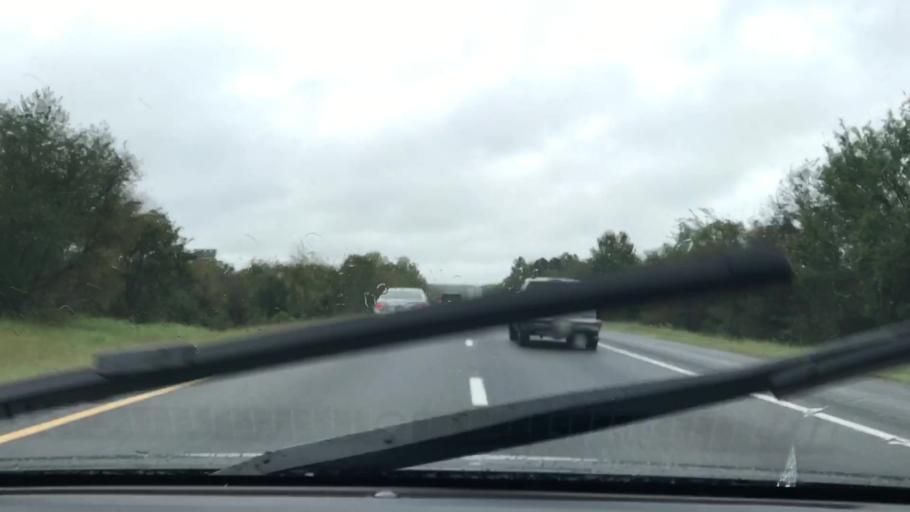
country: US
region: Tennessee
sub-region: Cheatham County
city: Pleasant View
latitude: 36.4760
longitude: -87.1412
